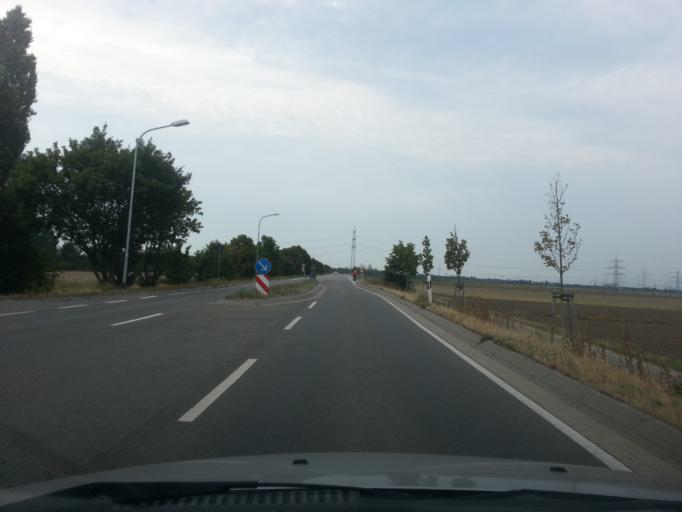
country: DE
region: Rheinland-Pfalz
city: Bobenheim-Roxheim
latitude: 49.5682
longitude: 8.3532
